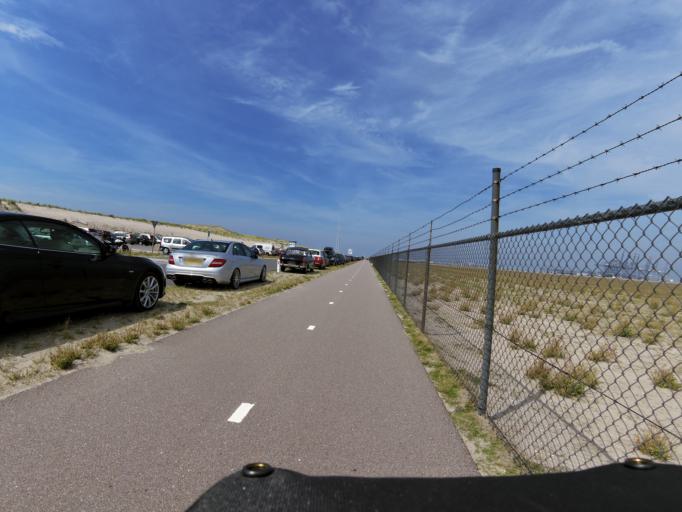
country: NL
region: South Holland
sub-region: Gemeente Goeree-Overflakkee
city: Goedereede
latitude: 51.9320
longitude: 3.9799
